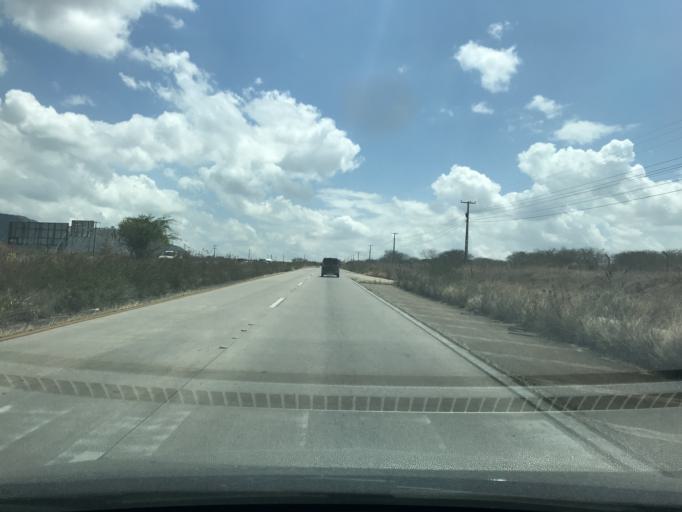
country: BR
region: Pernambuco
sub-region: Bezerros
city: Bezerros
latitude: -8.2923
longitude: -35.8241
